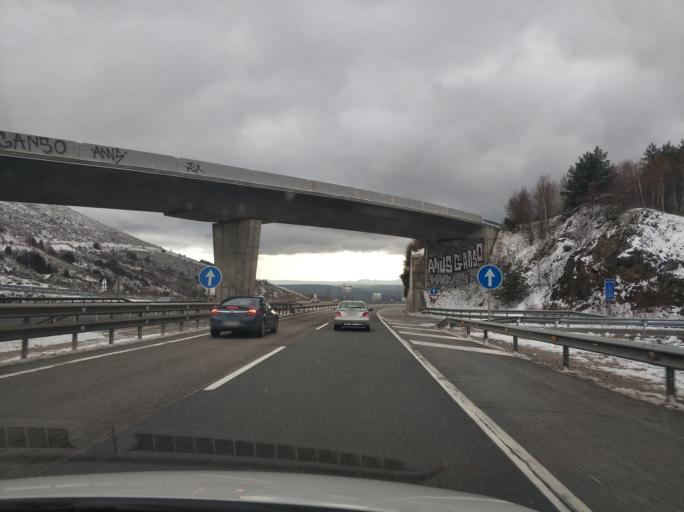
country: ES
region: Madrid
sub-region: Provincia de Madrid
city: Somosierra
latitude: 41.1201
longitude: -3.5864
